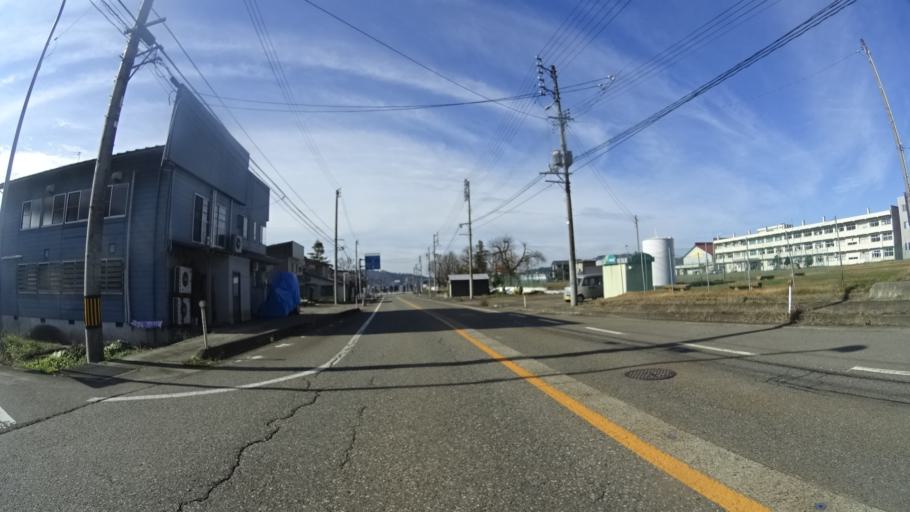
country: JP
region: Niigata
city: Muikamachi
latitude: 37.2284
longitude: 138.9869
